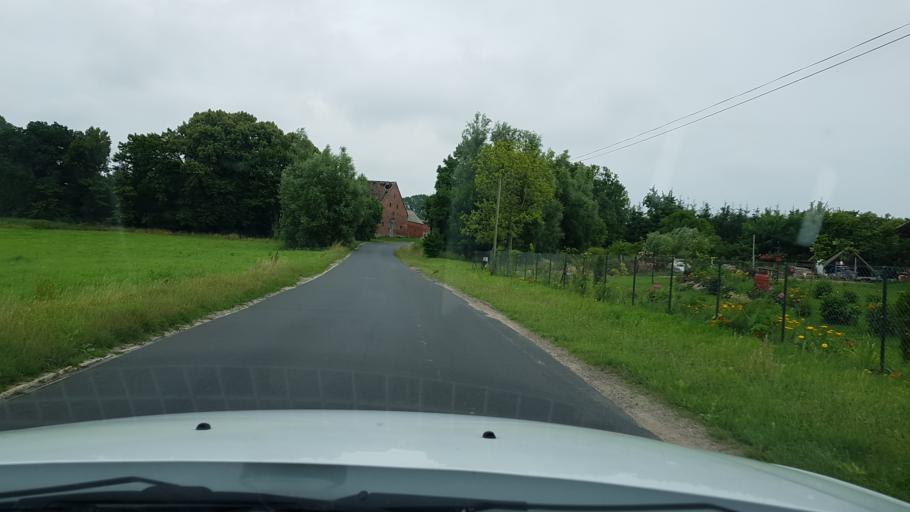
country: PL
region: West Pomeranian Voivodeship
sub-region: Powiat slawienski
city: Slawno
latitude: 54.4906
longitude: 16.5798
